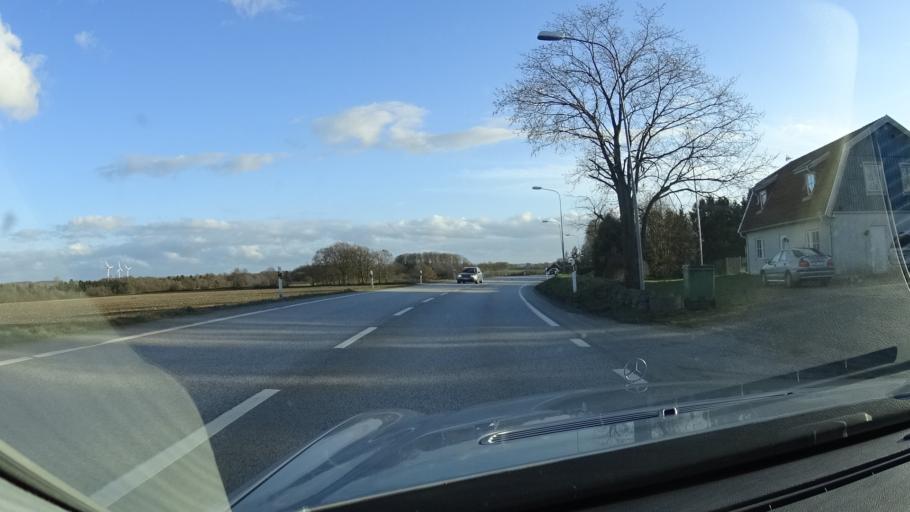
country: SE
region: Skane
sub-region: Hoors Kommun
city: Loberod
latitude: 55.8350
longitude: 13.4960
